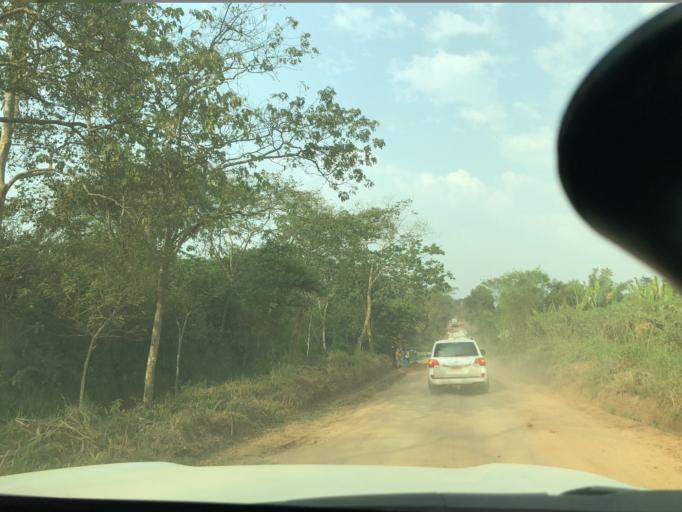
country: UG
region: Western Region
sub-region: Kasese District
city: Margherita
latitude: 0.1944
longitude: 29.6579
